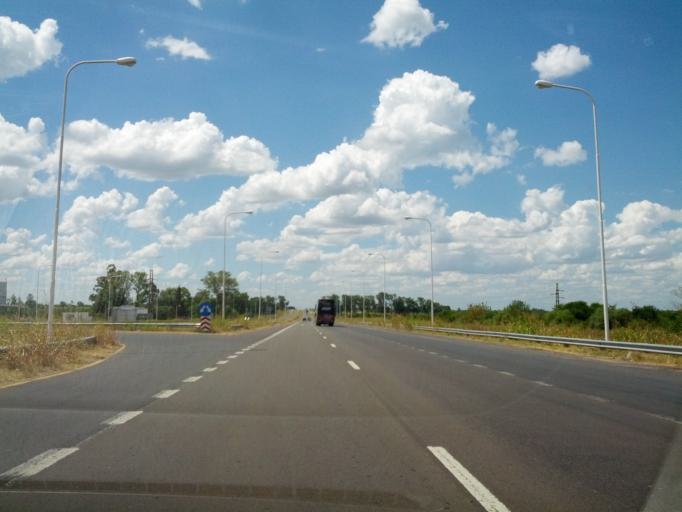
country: AR
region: Entre Rios
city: Concepcion del Uruguay
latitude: -32.4750
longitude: -58.3042
